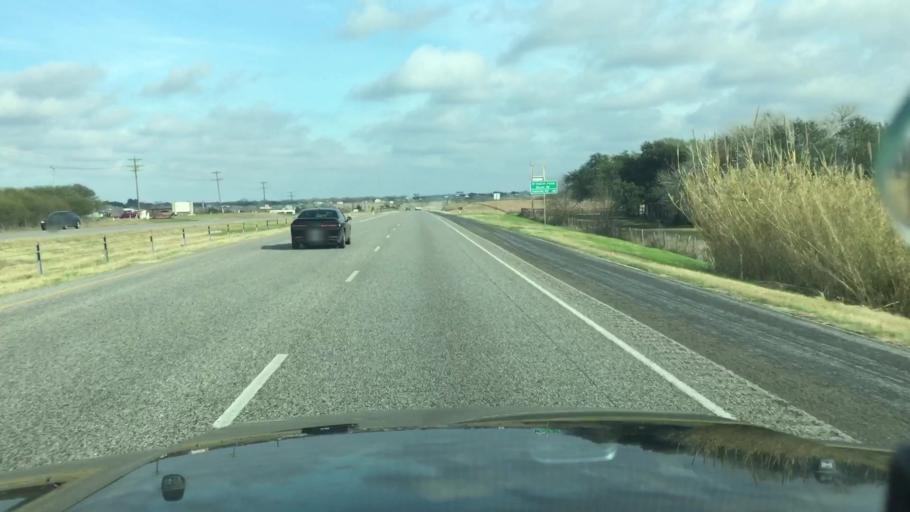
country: US
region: Texas
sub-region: Washington County
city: Brenham
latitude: 30.1383
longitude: -96.3187
